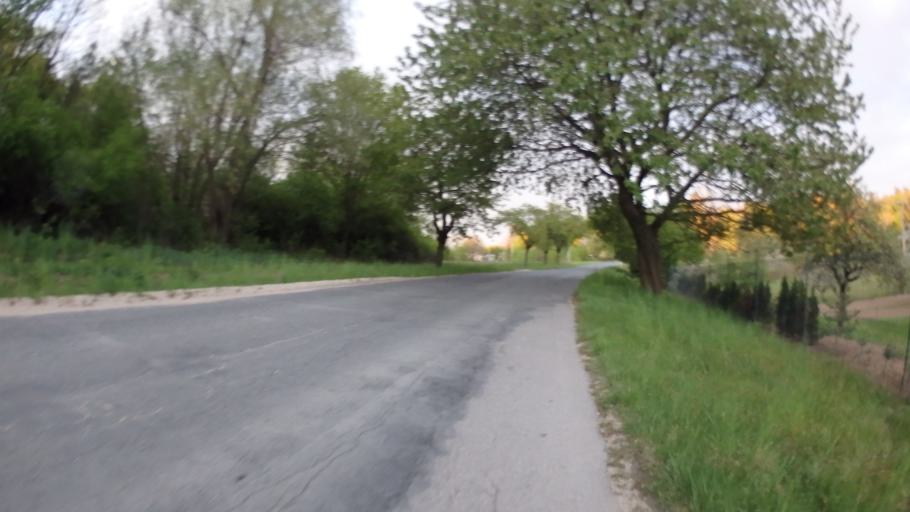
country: CZ
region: South Moravian
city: Strelice
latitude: 49.1519
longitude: 16.4707
